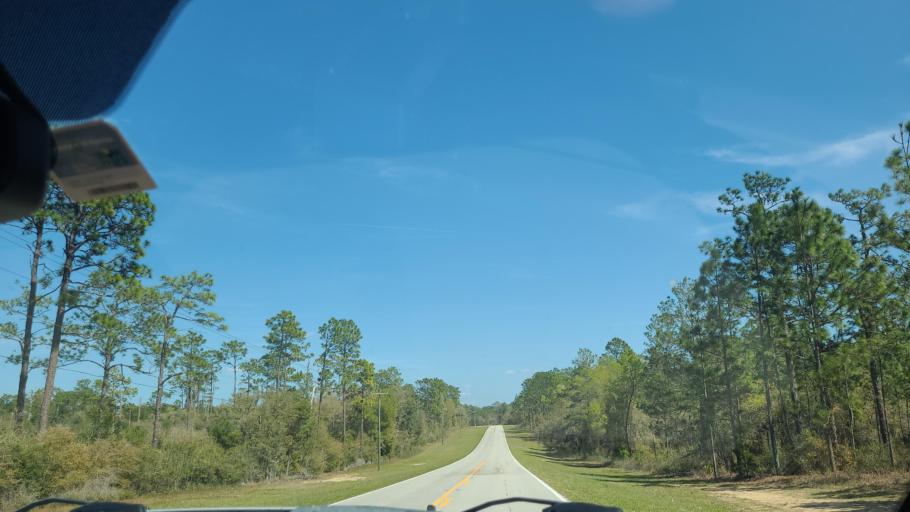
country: US
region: Florida
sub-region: Putnam County
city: Interlachen
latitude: 29.3663
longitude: -81.8152
